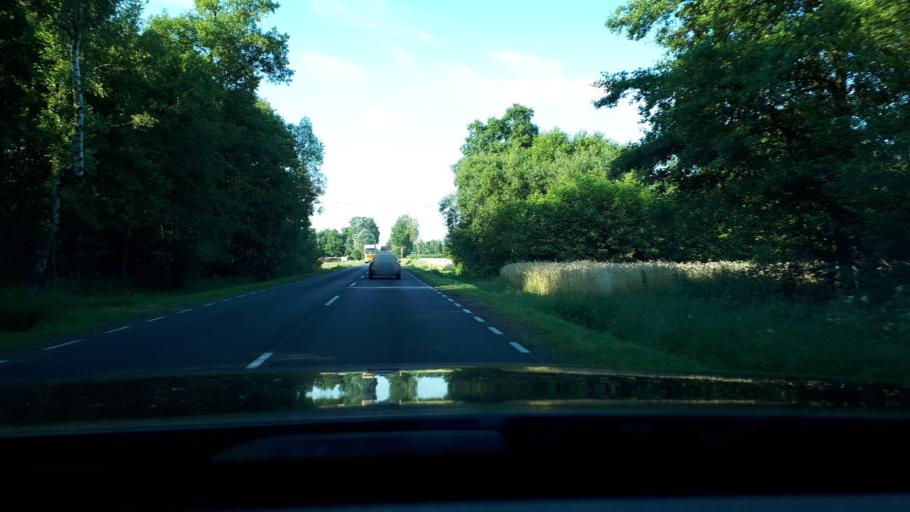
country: PL
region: Masovian Voivodeship
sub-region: Powiat plonski
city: Sochocin
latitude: 52.7121
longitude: 20.4970
